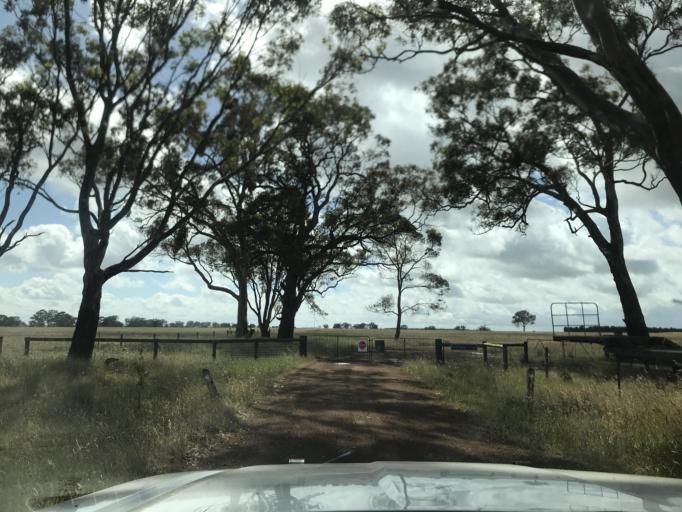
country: AU
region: South Australia
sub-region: Wattle Range
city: Penola
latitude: -37.2180
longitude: 141.3399
